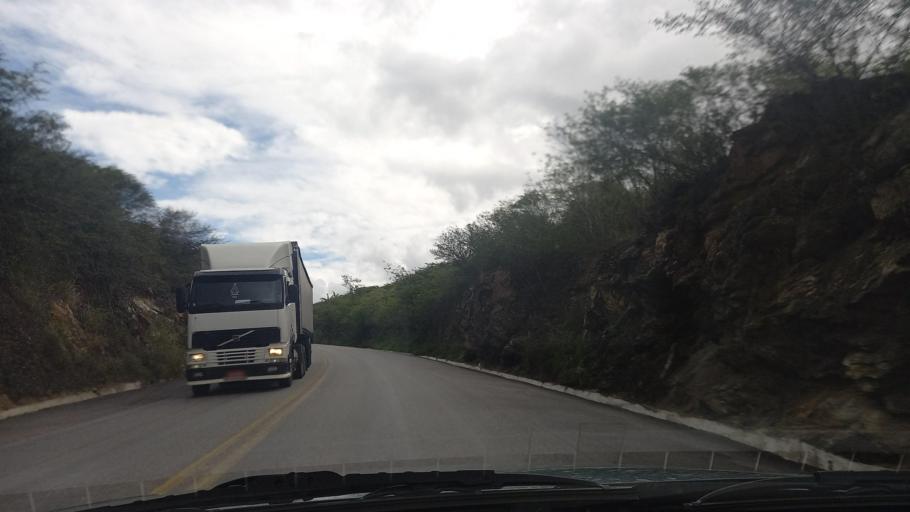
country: BR
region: Pernambuco
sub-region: Lajedo
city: Lajedo
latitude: -8.6739
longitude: -36.3990
